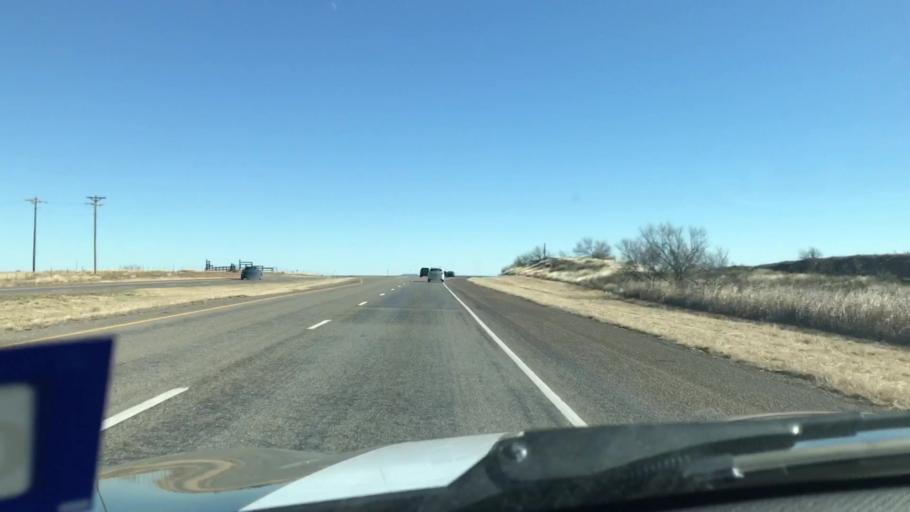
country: US
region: Texas
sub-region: Garza County
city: Post
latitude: 33.1389
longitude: -101.3145
